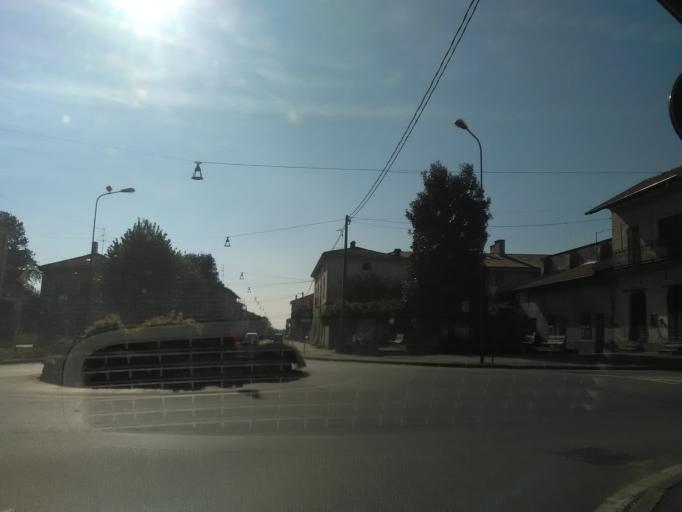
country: IT
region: Piedmont
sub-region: Provincia di Vercelli
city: Gattinara
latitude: 45.6112
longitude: 8.3720
